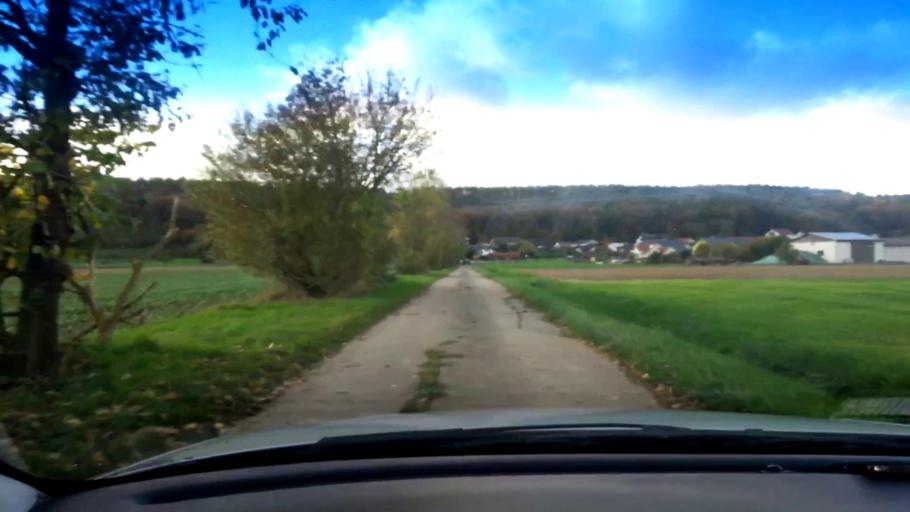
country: DE
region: Bavaria
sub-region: Upper Franconia
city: Zapfendorf
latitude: 50.0465
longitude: 10.9295
